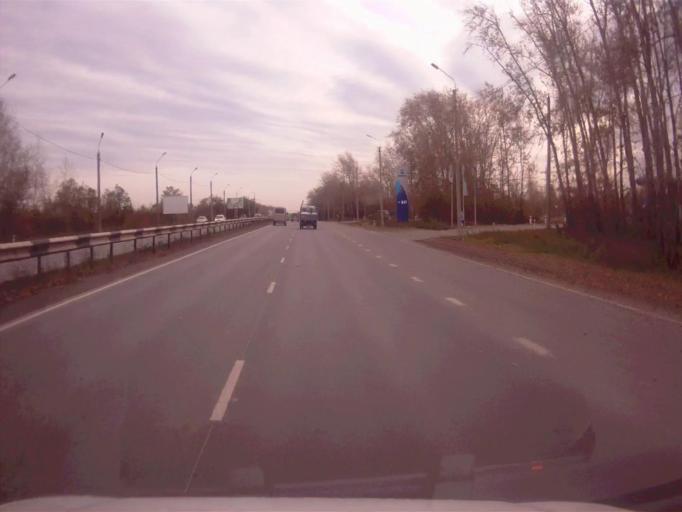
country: RU
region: Chelyabinsk
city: Novosineglazovskiy
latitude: 55.0542
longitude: 61.4088
